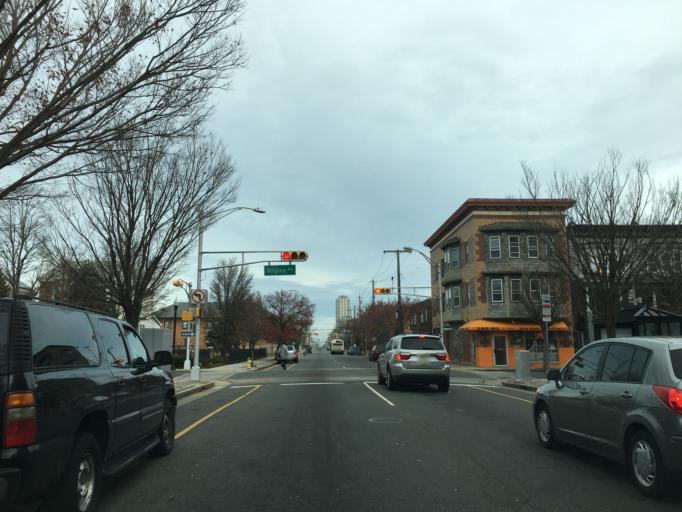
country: US
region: New Jersey
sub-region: Atlantic County
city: Atlantic City
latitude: 39.3656
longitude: -74.4245
